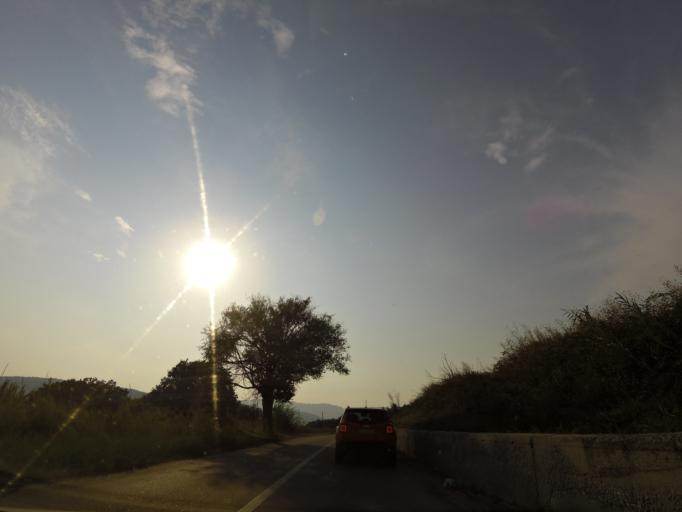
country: IT
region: Calabria
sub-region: Provincia di Reggio Calabria
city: Monasterace
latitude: 38.4396
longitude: 16.5467
